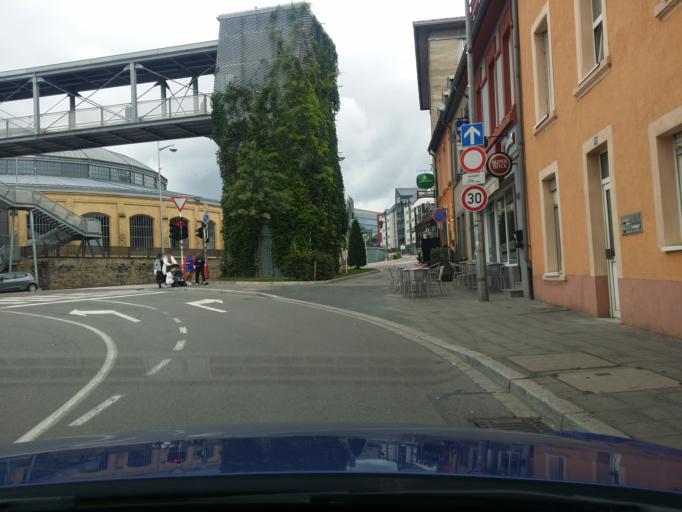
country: LU
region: Luxembourg
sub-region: Canton de Luxembourg
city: Luxembourg
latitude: 49.6003
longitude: 6.1371
